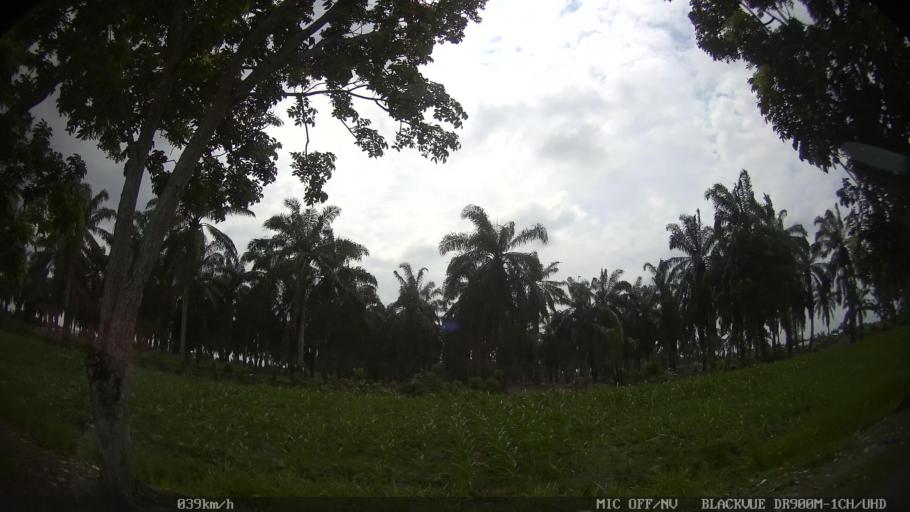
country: ID
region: North Sumatra
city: Sunggal
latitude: 3.6287
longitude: 98.6061
